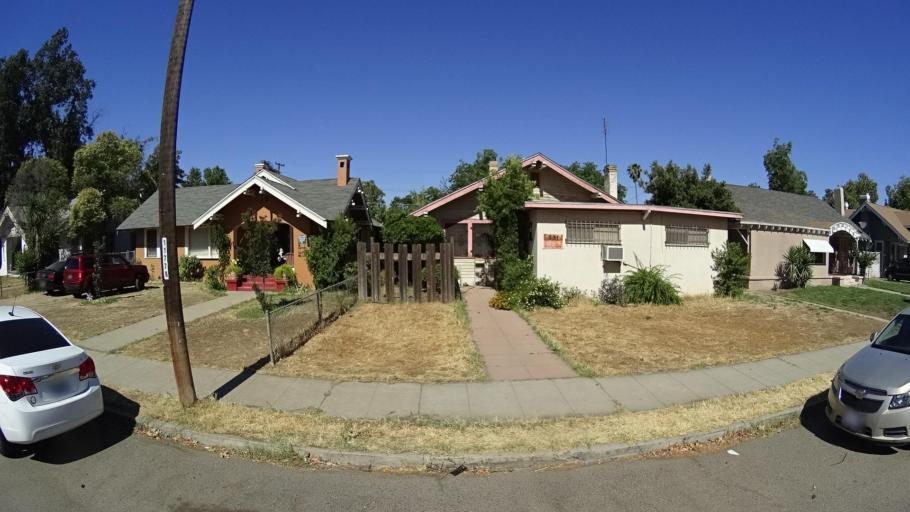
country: US
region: California
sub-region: Fresno County
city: Fresno
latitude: 36.7480
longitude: -119.8057
